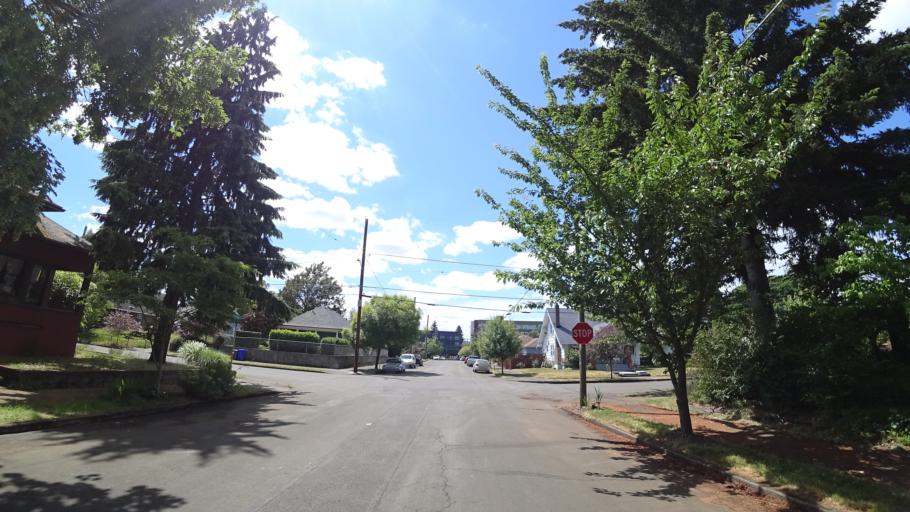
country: US
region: Oregon
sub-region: Multnomah County
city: Portland
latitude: 45.5605
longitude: -122.6798
